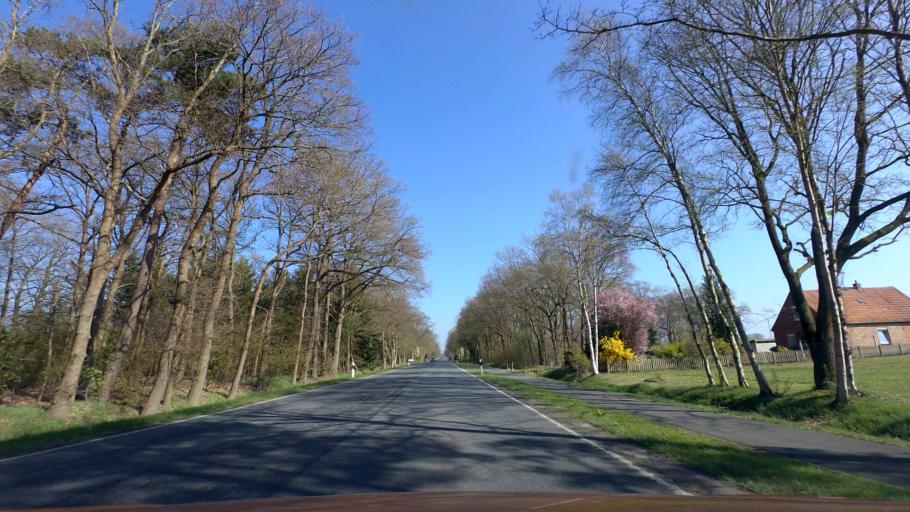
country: DE
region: Lower Saxony
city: Wardenburg
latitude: 53.0124
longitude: 8.1970
